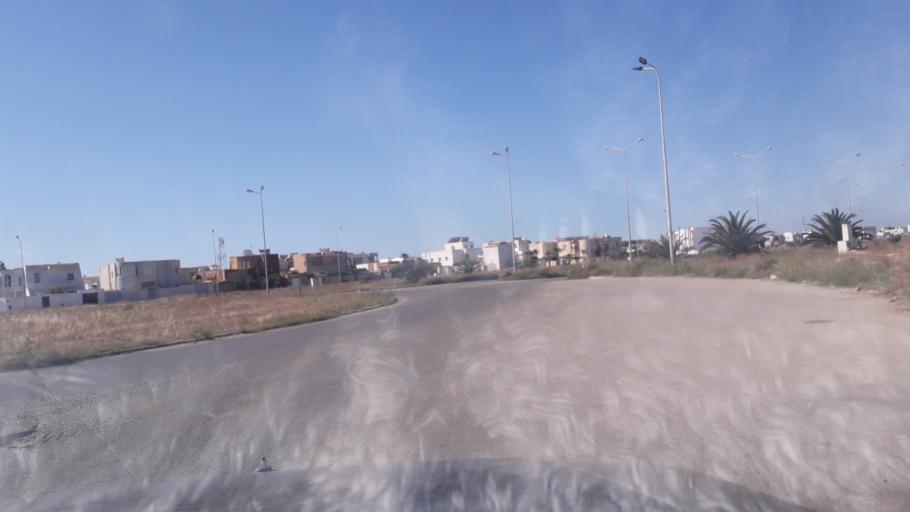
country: TN
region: Safaqis
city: Al Qarmadah
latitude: 34.8320
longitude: 10.7555
